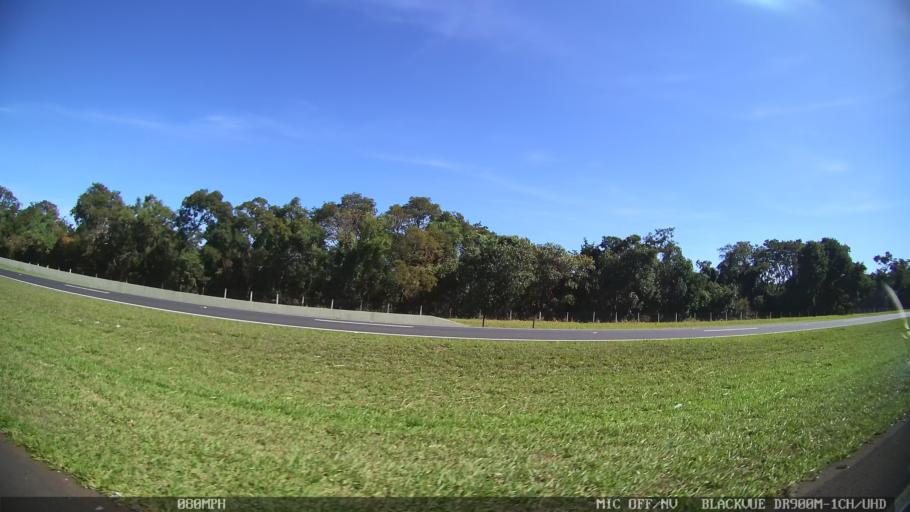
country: BR
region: Sao Paulo
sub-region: Santa Rita Do Passa Quatro
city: Santa Rita do Passa Quatro
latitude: -21.6288
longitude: -47.6139
